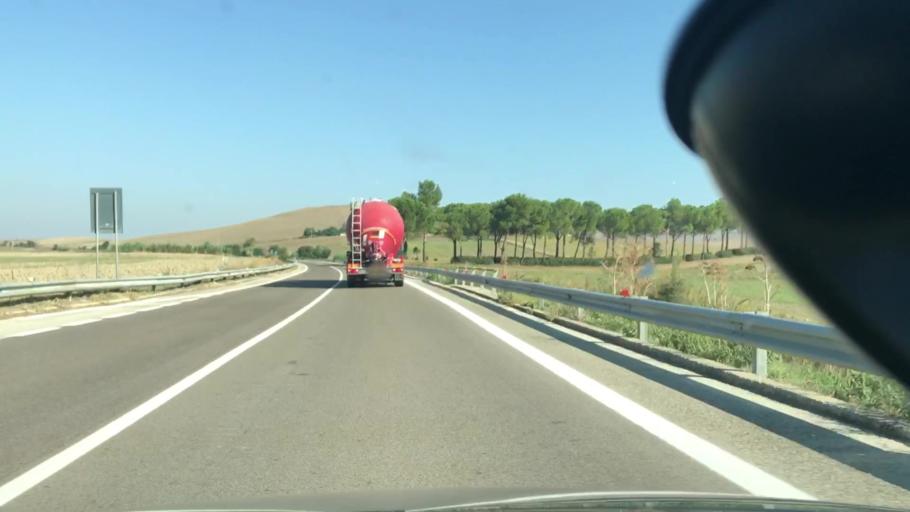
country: IT
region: Basilicate
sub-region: Provincia di Matera
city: Irsina
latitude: 40.8056
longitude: 16.2732
